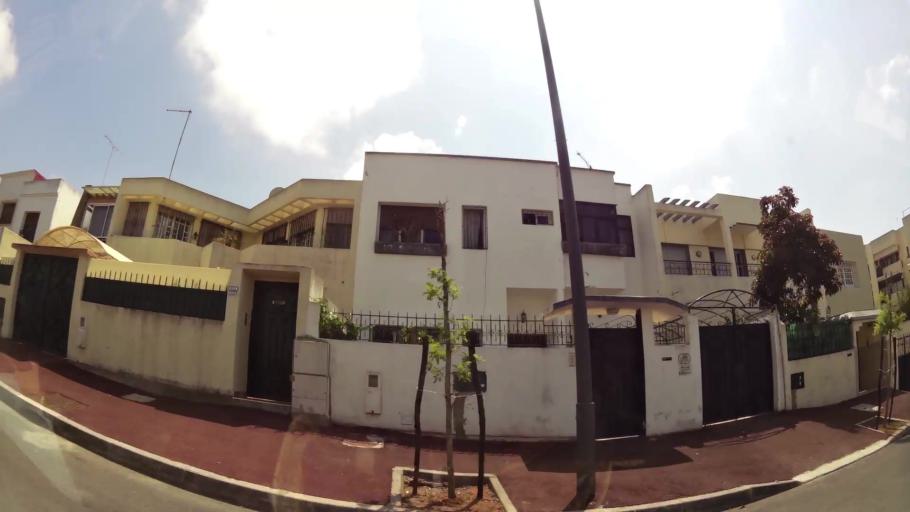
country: MA
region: Rabat-Sale-Zemmour-Zaer
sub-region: Skhirate-Temara
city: Temara
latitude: 33.9632
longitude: -6.8750
